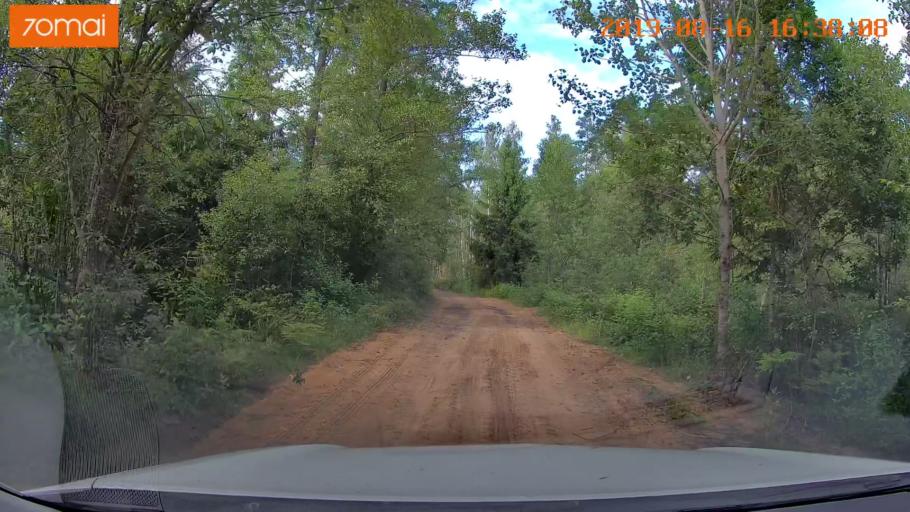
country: BY
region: Mogilev
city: Asipovichy
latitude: 53.2333
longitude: 28.7772
